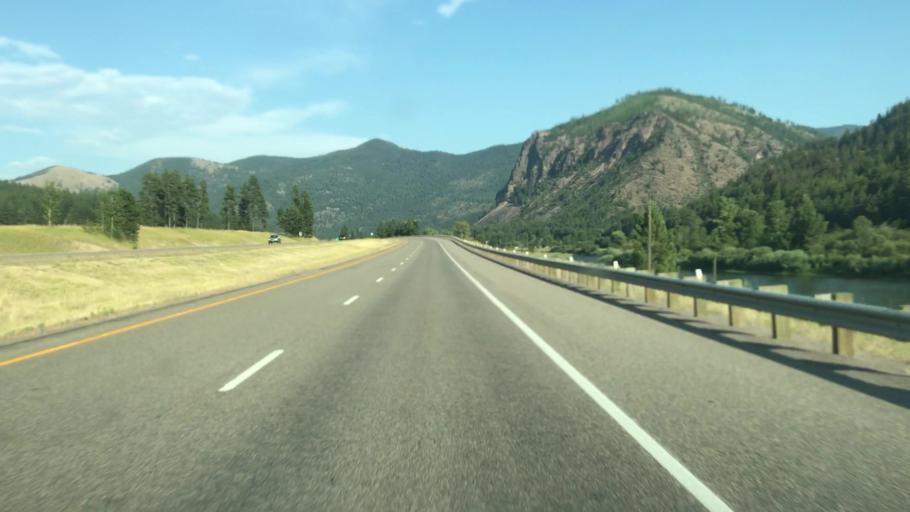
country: US
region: Montana
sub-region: Missoula County
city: Frenchtown
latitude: 46.9980
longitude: -114.4645
